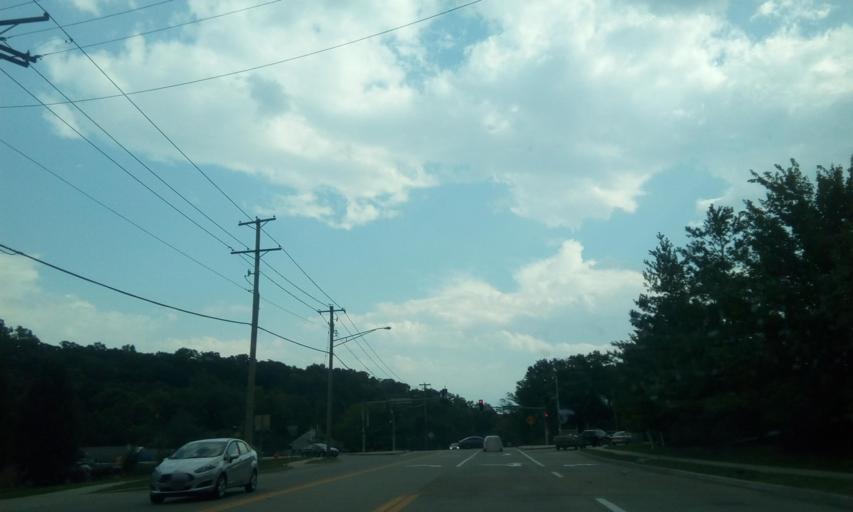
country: US
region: Missouri
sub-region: Saint Louis County
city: Town and Country
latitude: 38.5797
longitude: -90.4653
